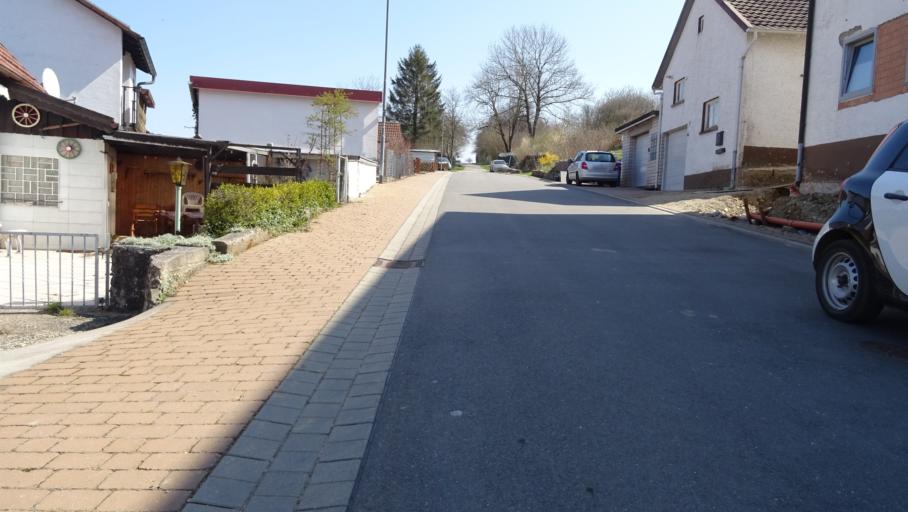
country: DE
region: Baden-Wuerttemberg
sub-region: Karlsruhe Region
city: Seckach
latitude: 49.4143
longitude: 9.2883
